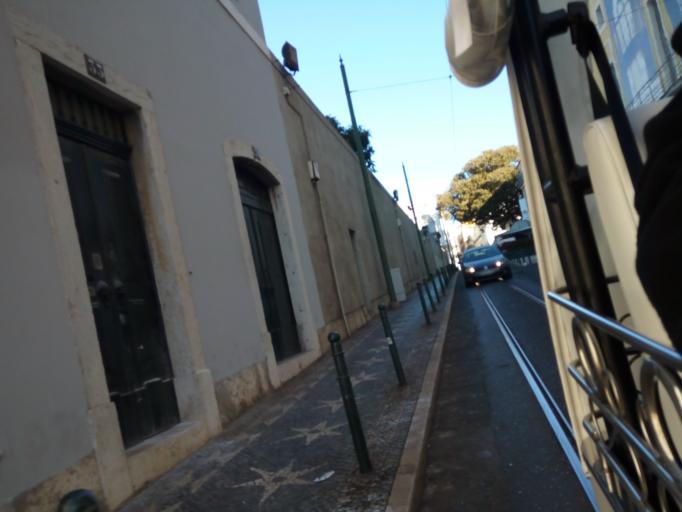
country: PT
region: Lisbon
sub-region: Lisbon
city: Lisbon
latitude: 38.7090
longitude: -9.1426
